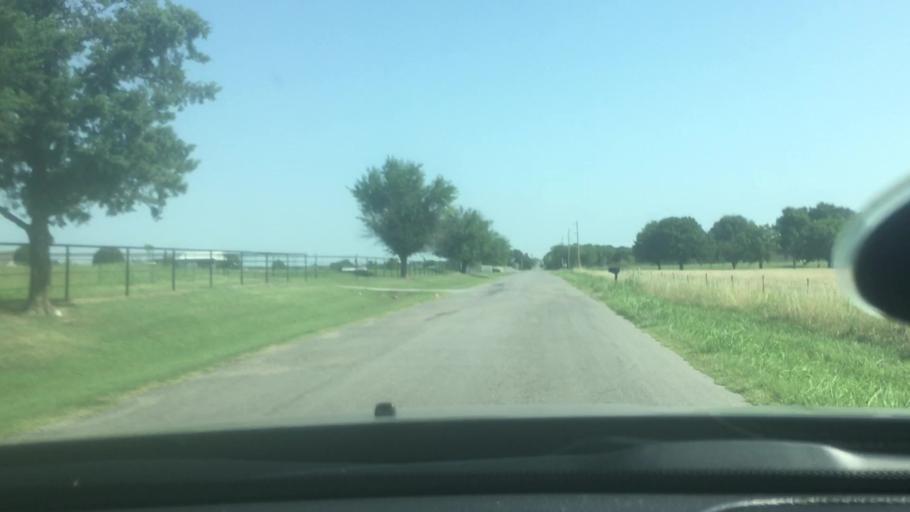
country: US
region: Oklahoma
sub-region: Bryan County
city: Calera
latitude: 33.9895
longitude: -96.4656
